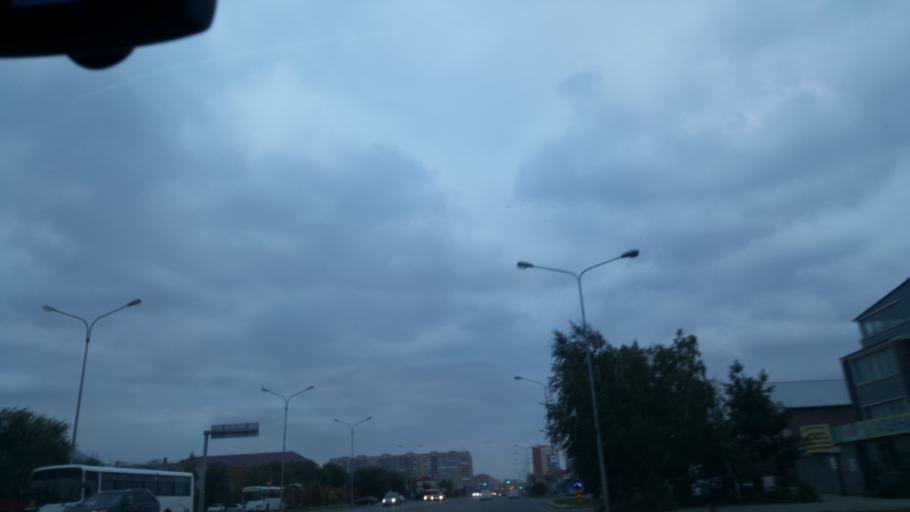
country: KZ
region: Astana Qalasy
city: Astana
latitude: 51.1372
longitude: 71.4912
